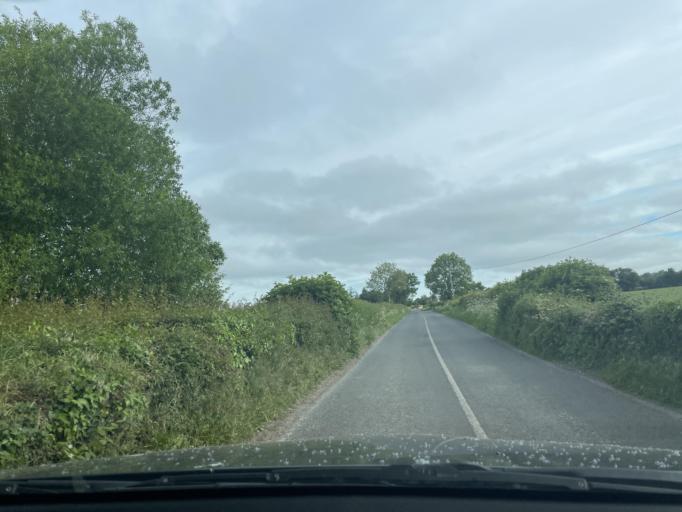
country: IE
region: Leinster
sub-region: County Carlow
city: Bagenalstown
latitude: 52.6477
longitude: -6.9728
